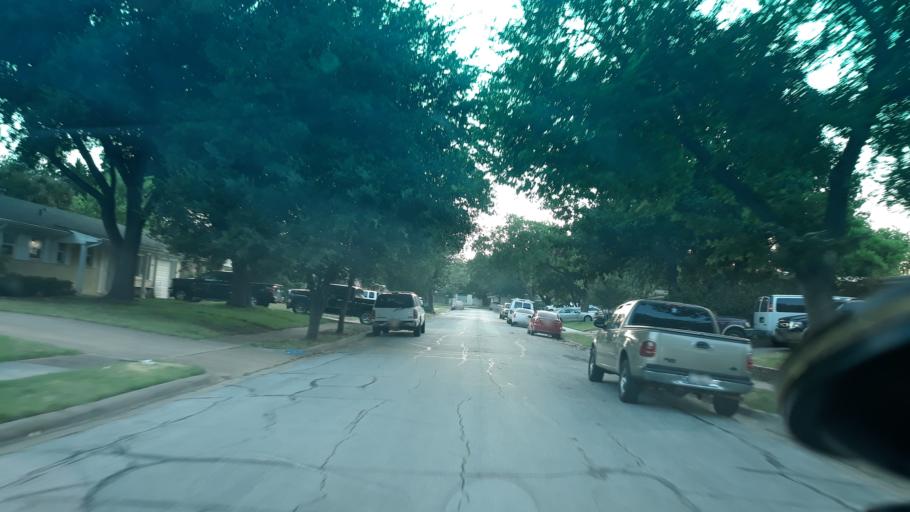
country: US
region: Texas
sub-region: Dallas County
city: Irving
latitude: 32.8363
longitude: -96.9825
